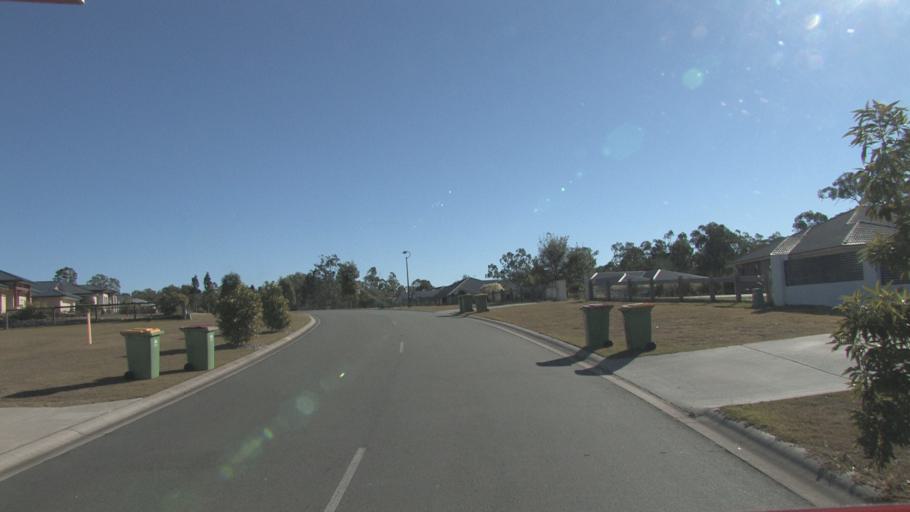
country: AU
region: Queensland
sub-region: Logan
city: North Maclean
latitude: -27.7508
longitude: 152.9681
